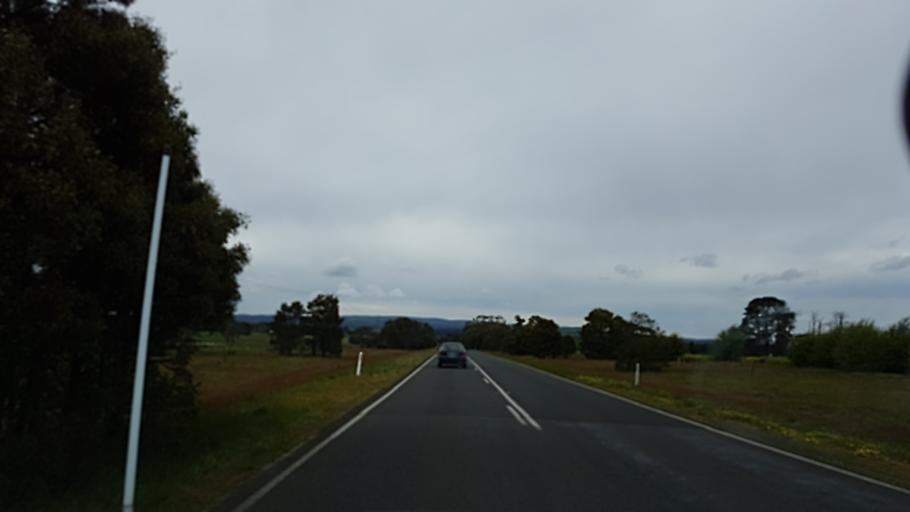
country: AU
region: Victoria
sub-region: Moorabool
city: Bacchus Marsh
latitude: -37.6154
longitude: 144.2127
